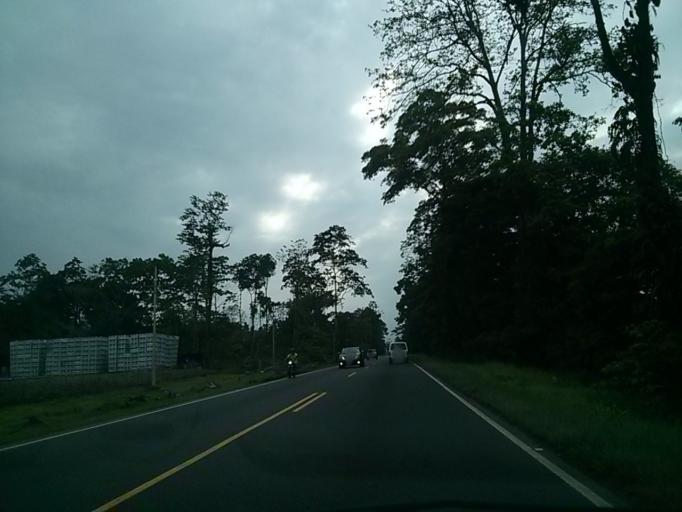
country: CR
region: Limon
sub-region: Canton de Pococi
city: Guapiles
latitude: 10.2042
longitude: -83.7592
